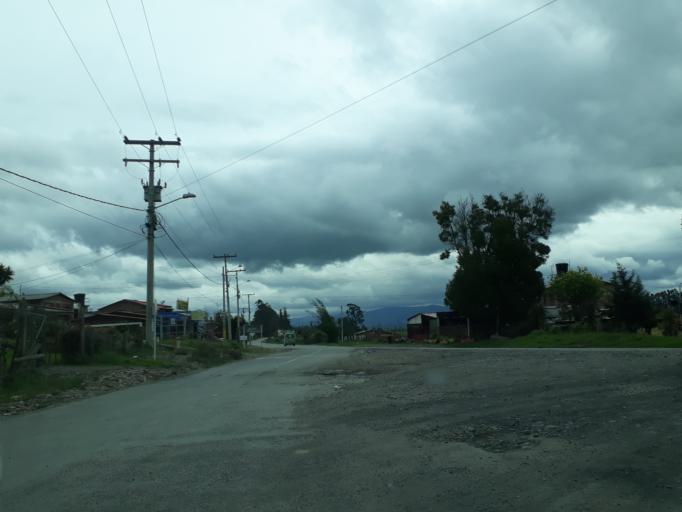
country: CO
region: Cundinamarca
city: Simijaca
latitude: 5.5190
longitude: -73.8377
